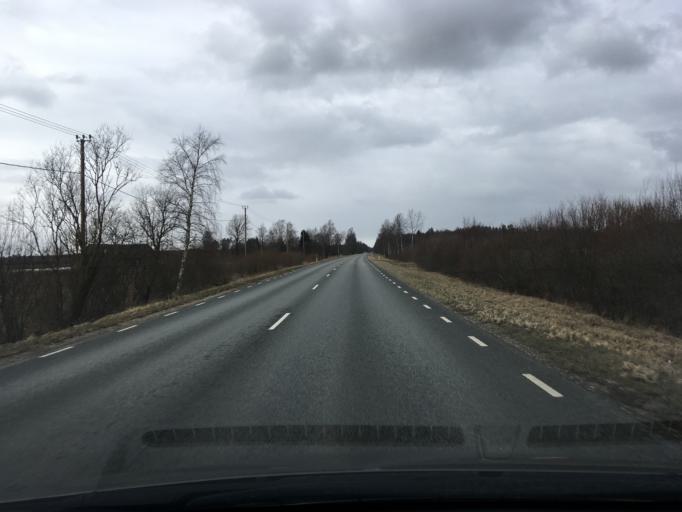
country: EE
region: Laeaene
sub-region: Lihula vald
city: Lihula
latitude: 58.6350
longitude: 23.8652
